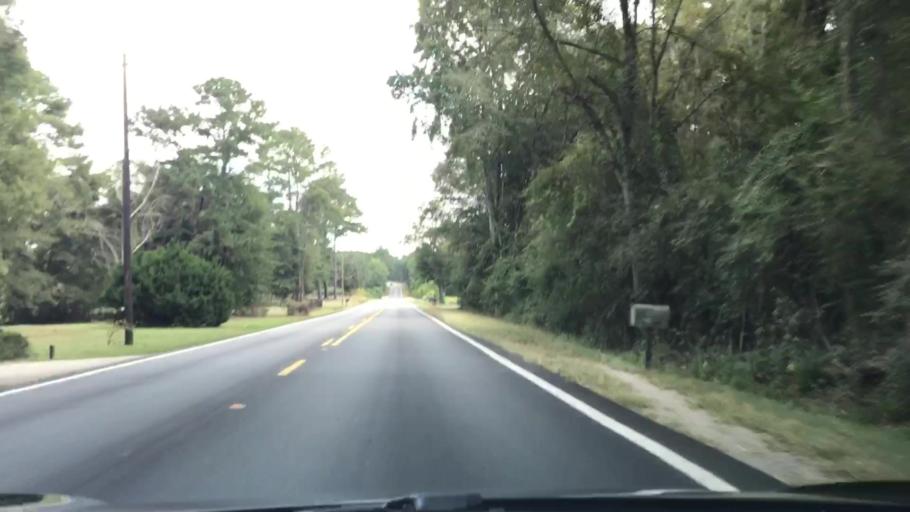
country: US
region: Georgia
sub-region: Greene County
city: Greensboro
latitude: 33.5634
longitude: -83.1439
